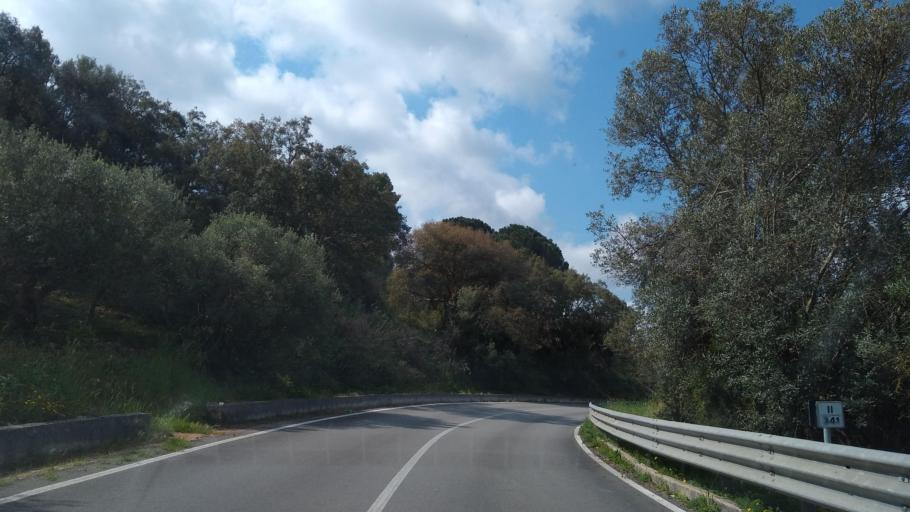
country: IT
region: Sicily
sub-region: Trapani
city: Calatafimi
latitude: 37.9544
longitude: 12.8654
